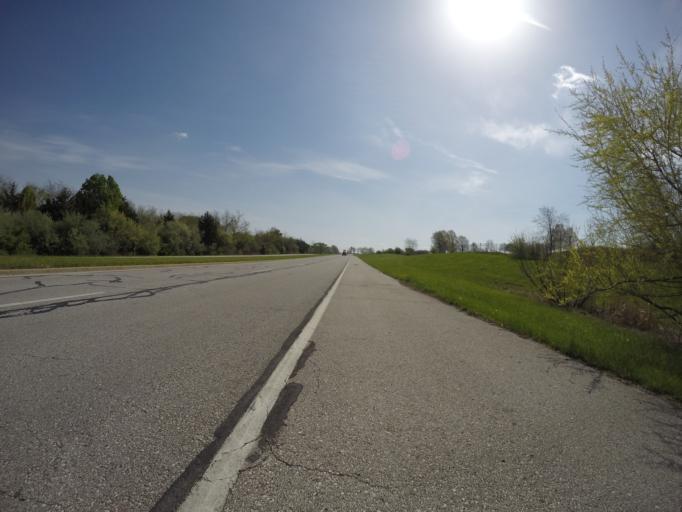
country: US
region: Missouri
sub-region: Jackson County
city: Lees Summit
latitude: 38.9240
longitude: -94.4580
